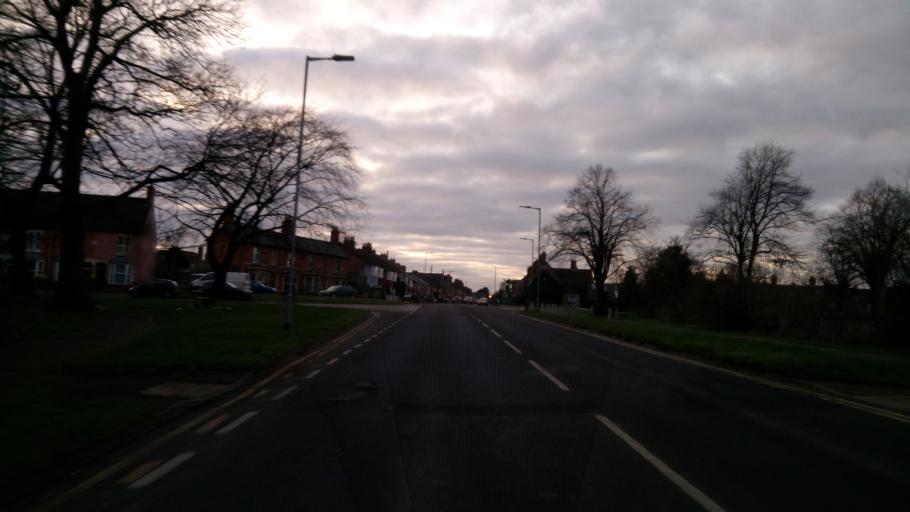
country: GB
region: England
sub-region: Peterborough
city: Peterborough
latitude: 52.5594
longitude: -0.2351
